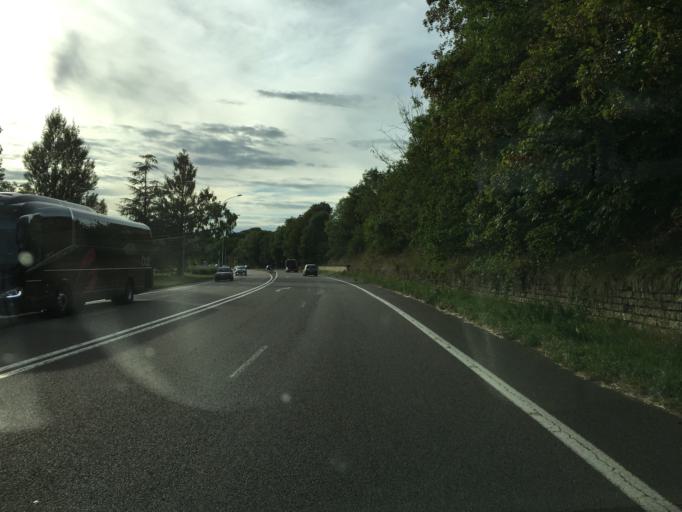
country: FR
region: Bourgogne
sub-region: Departement de la Cote-d'Or
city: Talant
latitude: 47.3294
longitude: 5.0014
